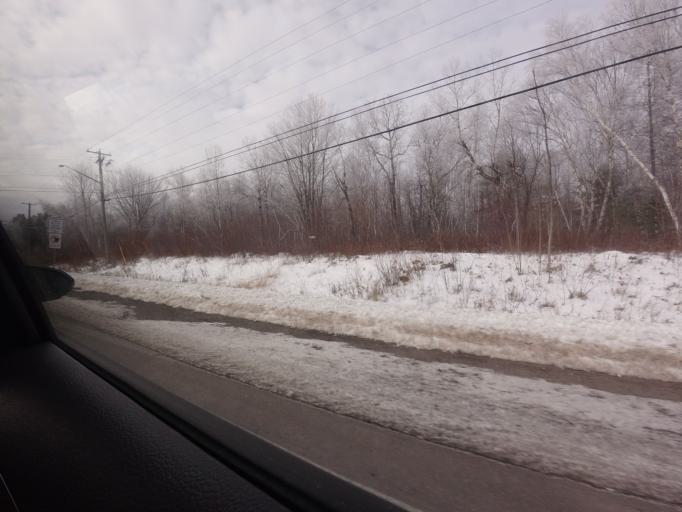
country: CA
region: New Brunswick
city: Oromocto
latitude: 45.8593
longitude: -66.4518
